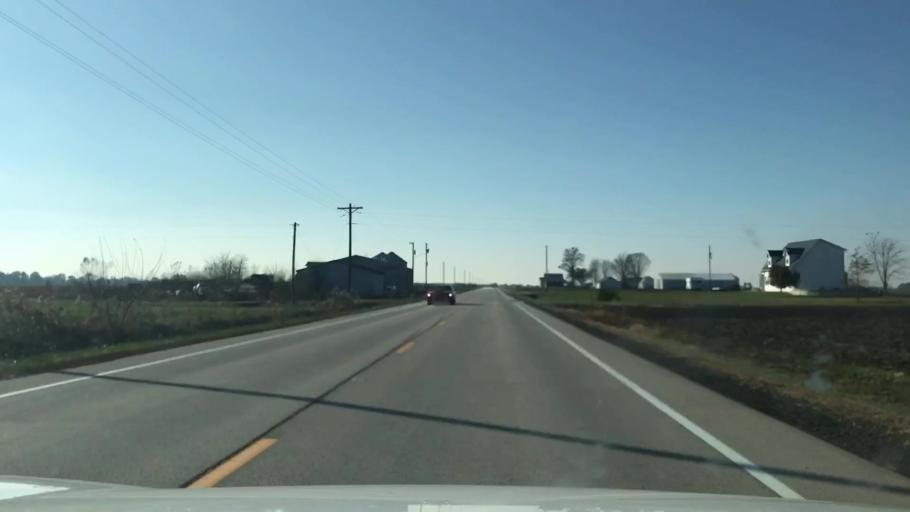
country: US
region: Illinois
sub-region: Washington County
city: Okawville
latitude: 38.4425
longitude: -89.5041
